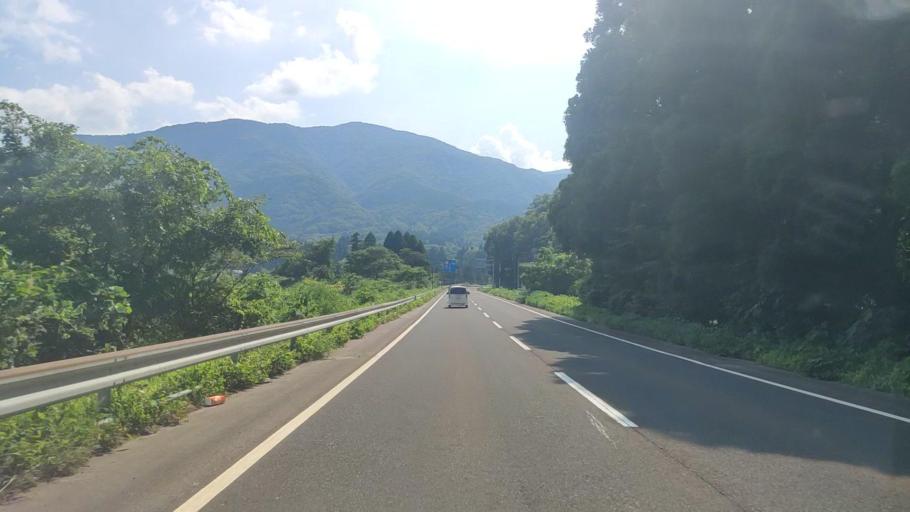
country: JP
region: Fukui
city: Tsuruga
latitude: 35.6035
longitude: 136.1053
